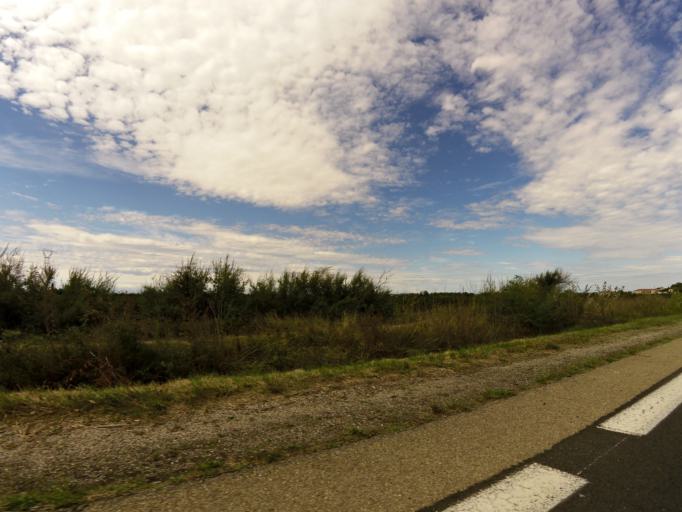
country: FR
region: Languedoc-Roussillon
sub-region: Departement du Gard
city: Aimargues
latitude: 43.6638
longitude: 4.2096
